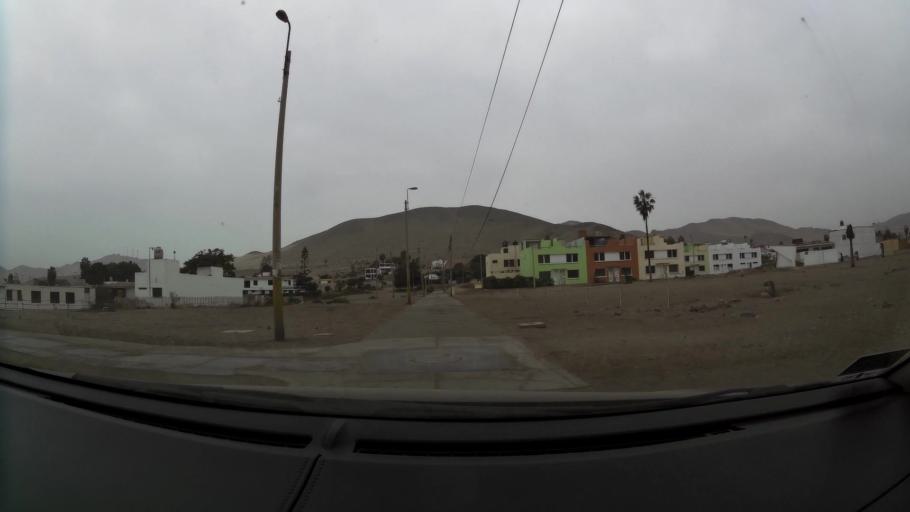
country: PE
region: Lima
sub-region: Lima
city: Santa Rosa
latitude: -11.7966
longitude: -77.1757
